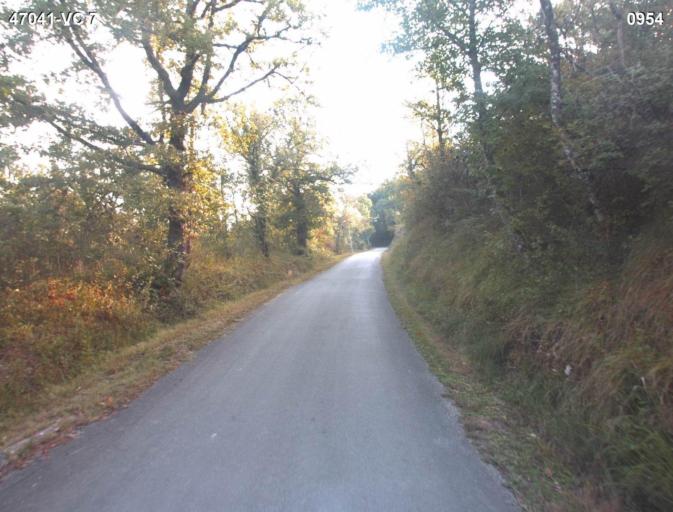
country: FR
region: Aquitaine
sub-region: Departement du Lot-et-Garonne
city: Port-Sainte-Marie
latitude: 44.1981
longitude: 0.4120
